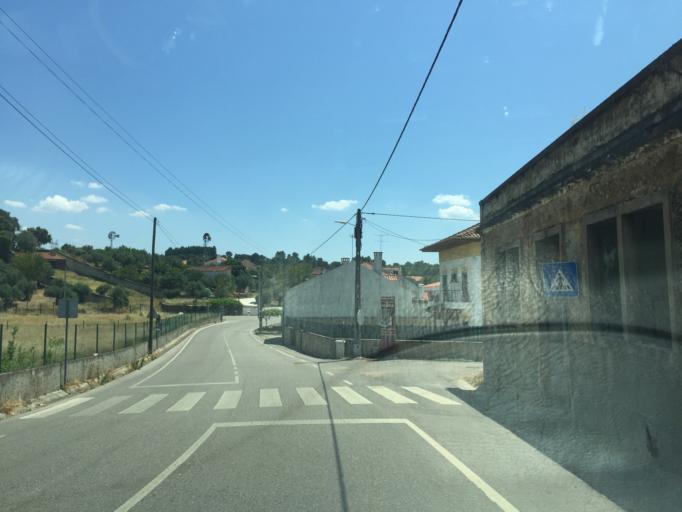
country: PT
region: Santarem
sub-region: Tomar
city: Tomar
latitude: 39.5962
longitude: -8.3251
